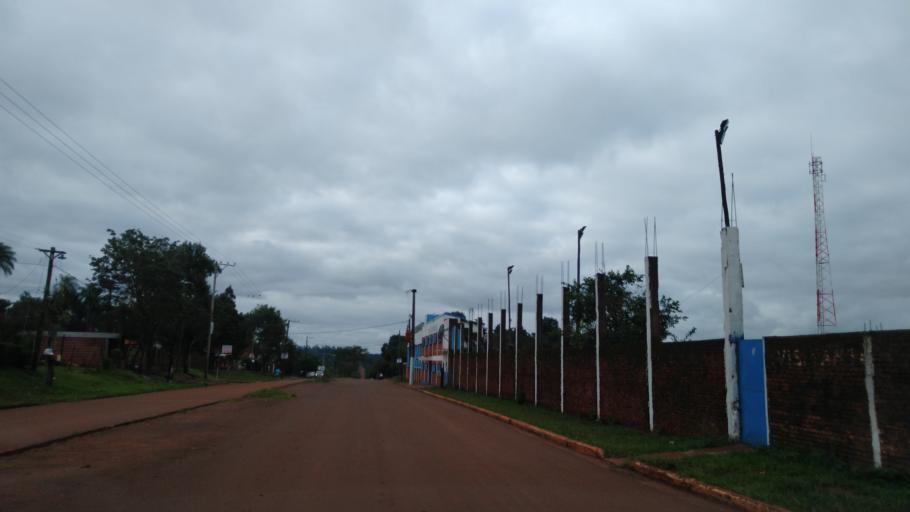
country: AR
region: Misiones
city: Jardin America
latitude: -27.0322
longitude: -55.2349
